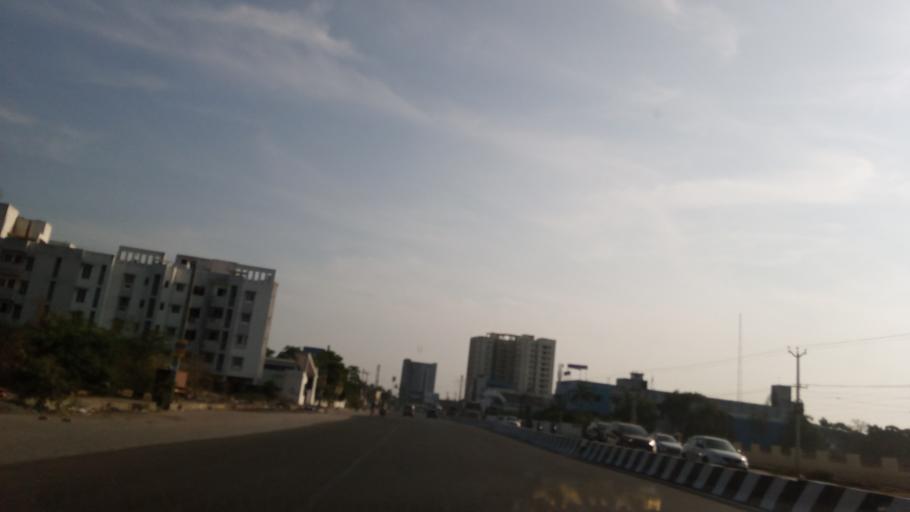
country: IN
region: Tamil Nadu
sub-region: Kancheepuram
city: Poonamalle
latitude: 13.0509
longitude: 80.1223
